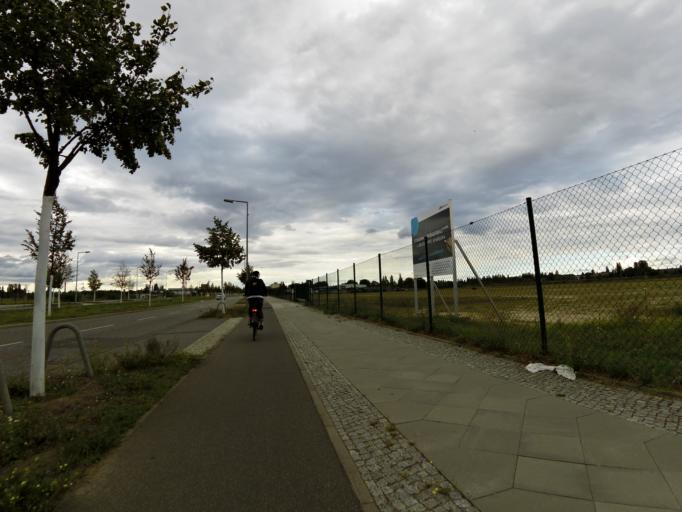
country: DE
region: Berlin
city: Niederschoneweide
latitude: 52.4384
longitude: 13.5264
